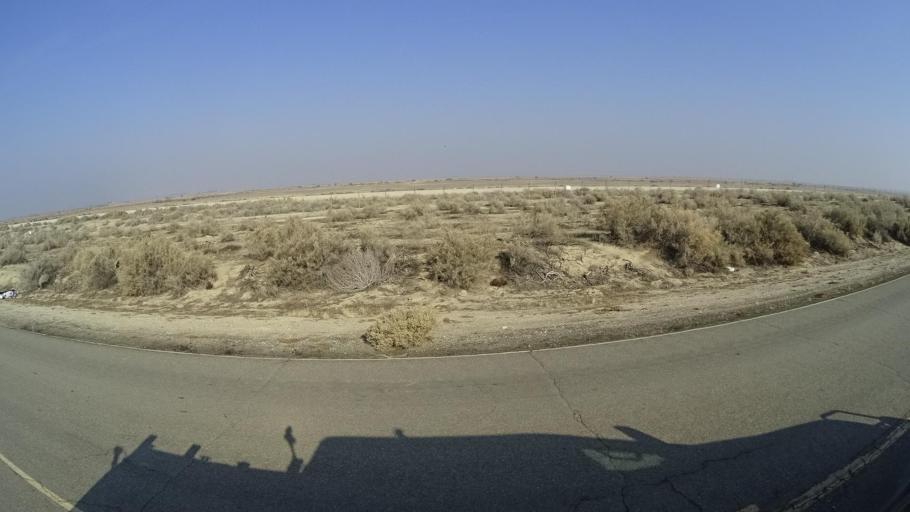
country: US
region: California
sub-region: Kern County
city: Buttonwillow
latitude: 35.3033
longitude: -119.3647
